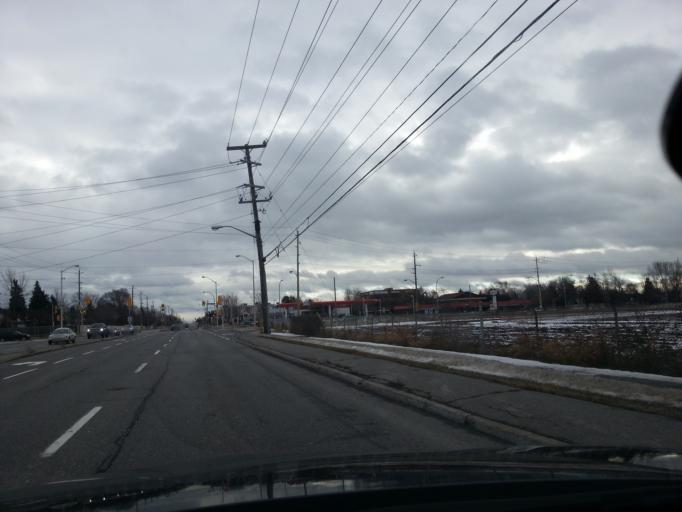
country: CA
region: Ontario
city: Bells Corners
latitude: 45.2891
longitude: -75.7577
